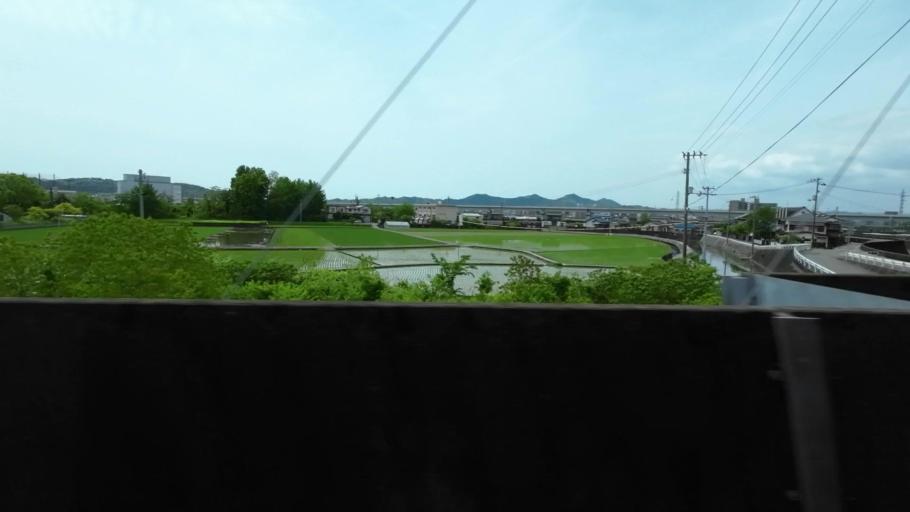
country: JP
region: Kochi
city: Kochi-shi
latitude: 33.5806
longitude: 133.5736
